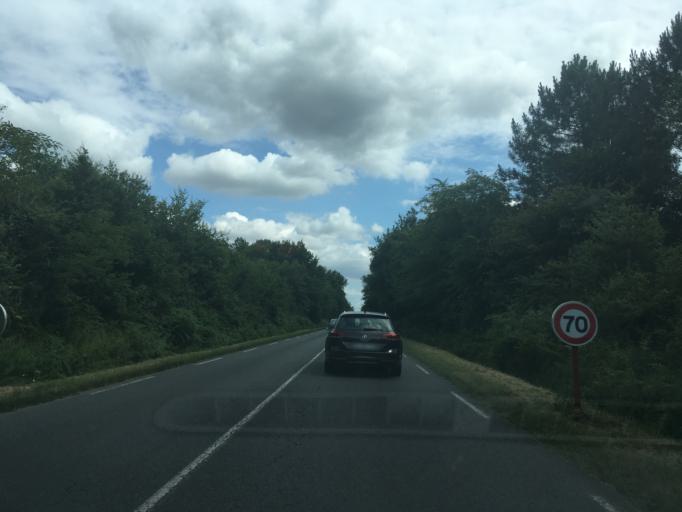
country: FR
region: Aquitaine
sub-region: Departement de la Gironde
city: Le Taillan-Medoc
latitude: 44.9206
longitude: -0.6731
